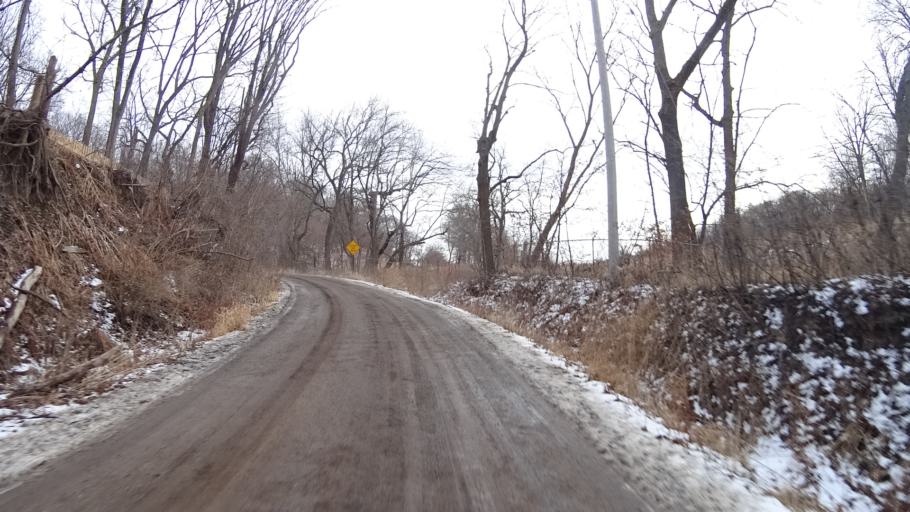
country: US
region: Nebraska
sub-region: Sarpy County
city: Bellevue
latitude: 41.1723
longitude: -95.9070
